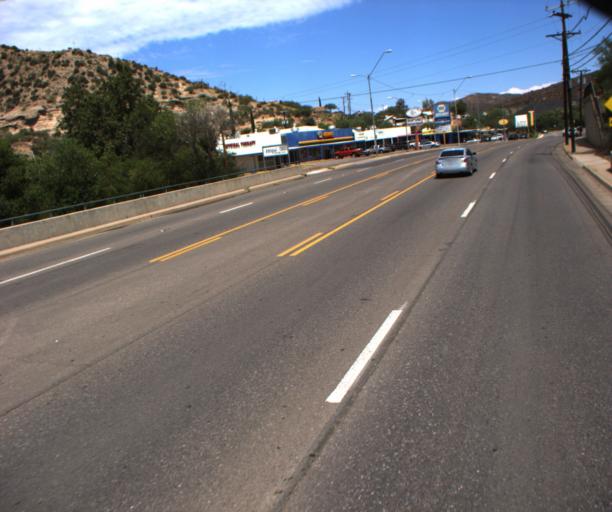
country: US
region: Arizona
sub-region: Gila County
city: Globe
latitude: 33.4051
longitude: -110.7929
